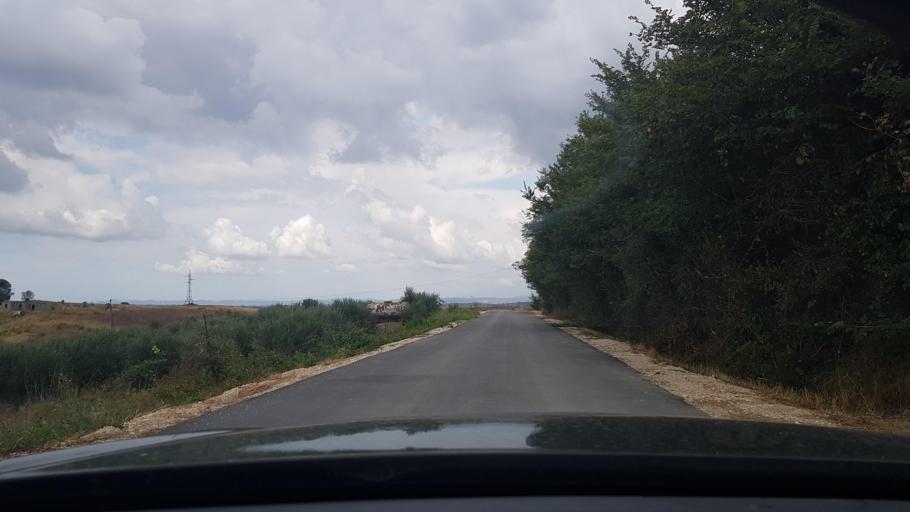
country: AL
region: Durres
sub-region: Rrethi i Durresit
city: Gjepalaj
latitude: 41.3043
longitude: 19.5537
